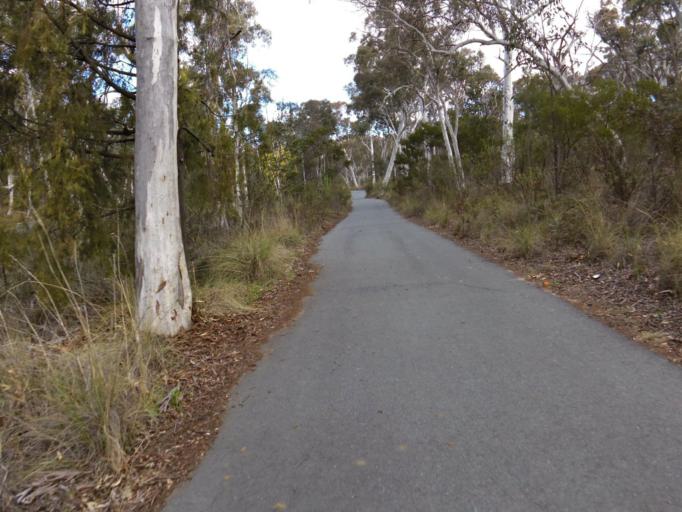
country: AU
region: Australian Capital Territory
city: Macquarie
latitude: -35.2500
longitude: 149.0933
